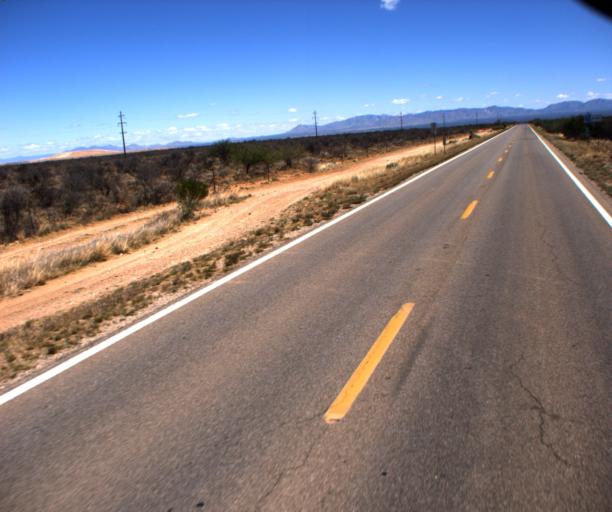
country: US
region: Arizona
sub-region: Cochise County
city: Huachuca City
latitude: 31.7016
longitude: -110.2952
